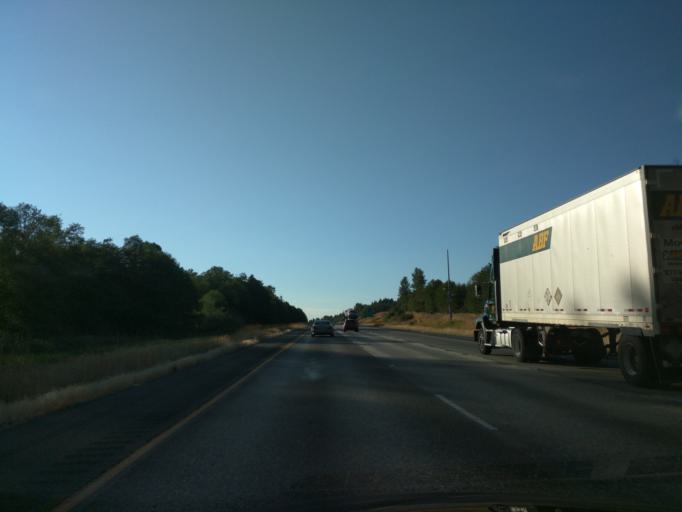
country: US
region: Washington
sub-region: Snohomish County
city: Bryant
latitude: 48.2525
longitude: -122.2536
